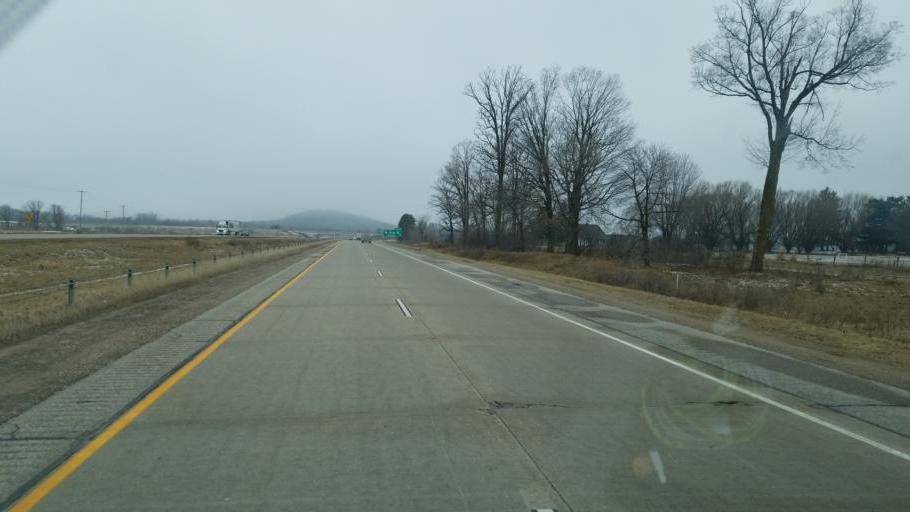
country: US
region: Wisconsin
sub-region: Waupaca County
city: Waupaca
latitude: 44.3295
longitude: -89.0320
